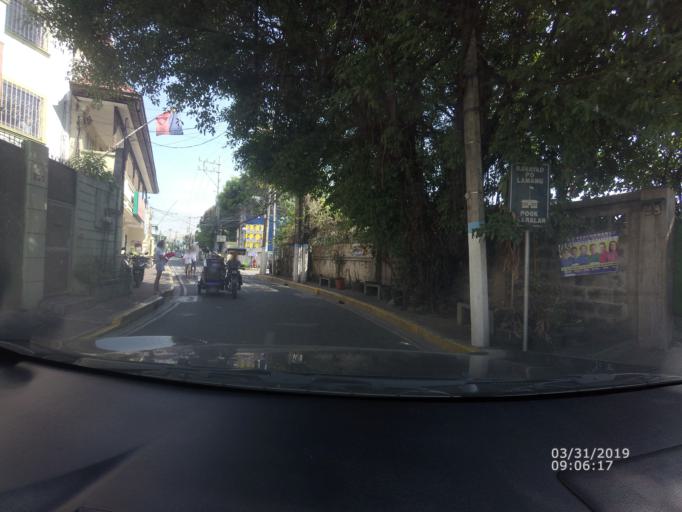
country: PH
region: Metro Manila
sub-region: San Juan
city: San Juan
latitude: 14.5853
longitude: 121.0214
